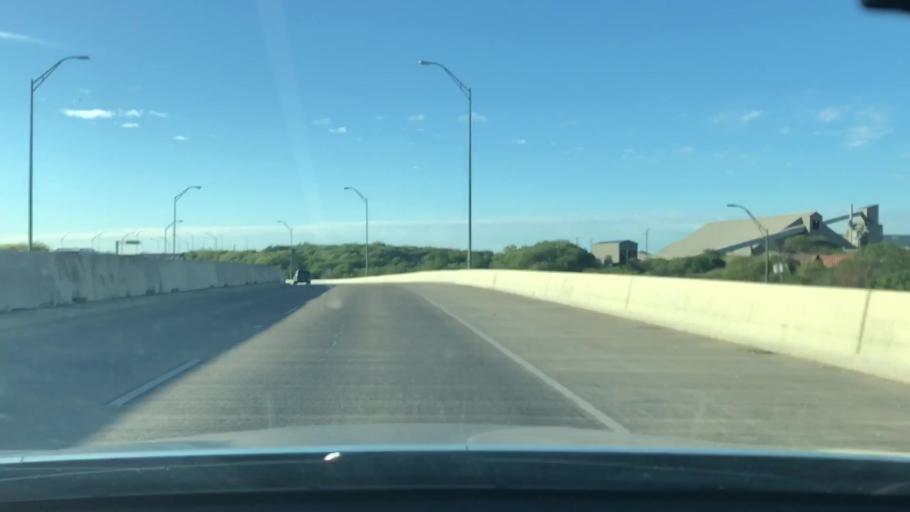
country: US
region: Texas
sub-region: Bexar County
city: Windcrest
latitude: 29.5407
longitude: -98.4211
